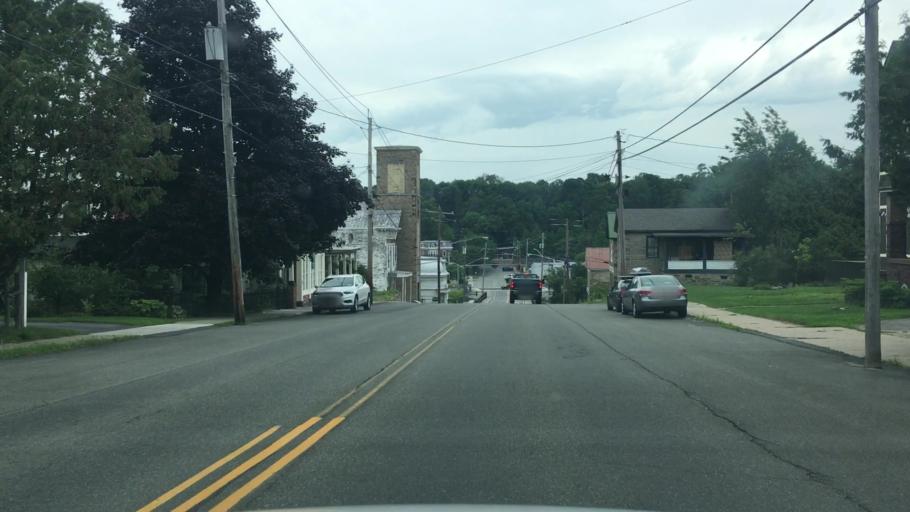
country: US
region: New York
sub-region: Essex County
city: Keeseville
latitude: 44.5057
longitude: -73.4829
